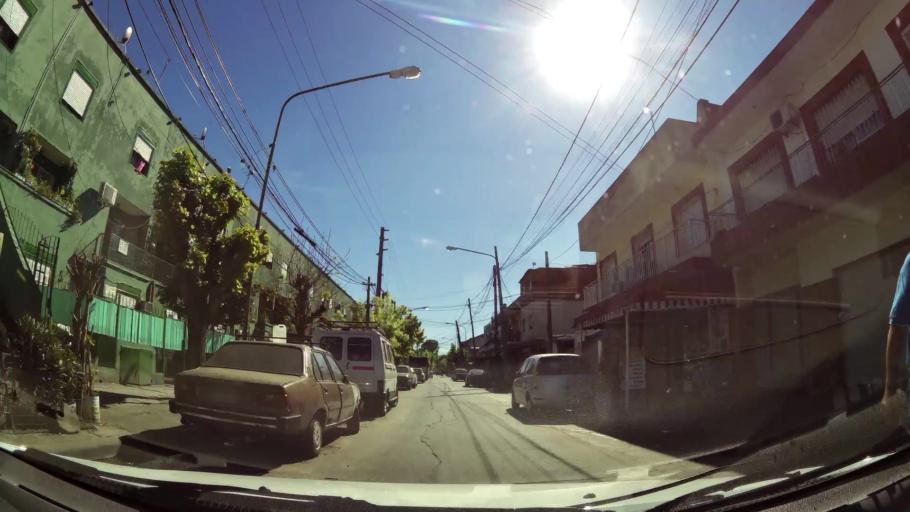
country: AR
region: Buenos Aires
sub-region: Partido de General San Martin
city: General San Martin
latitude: -34.5496
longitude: -58.5230
